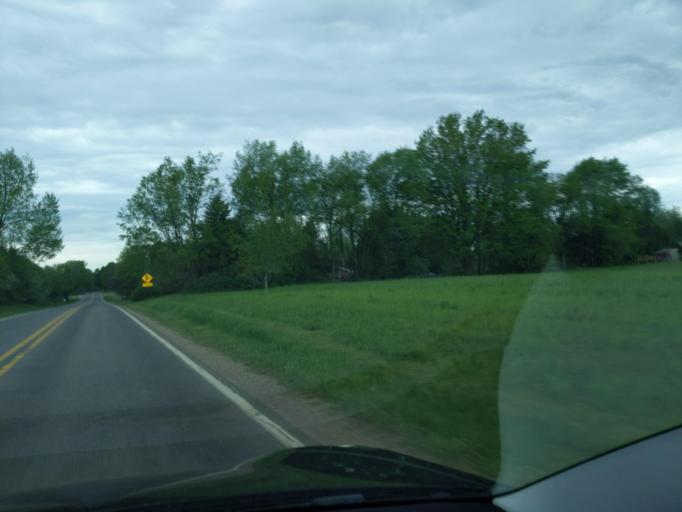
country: US
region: Michigan
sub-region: Ingham County
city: Mason
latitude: 42.5320
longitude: -84.3215
